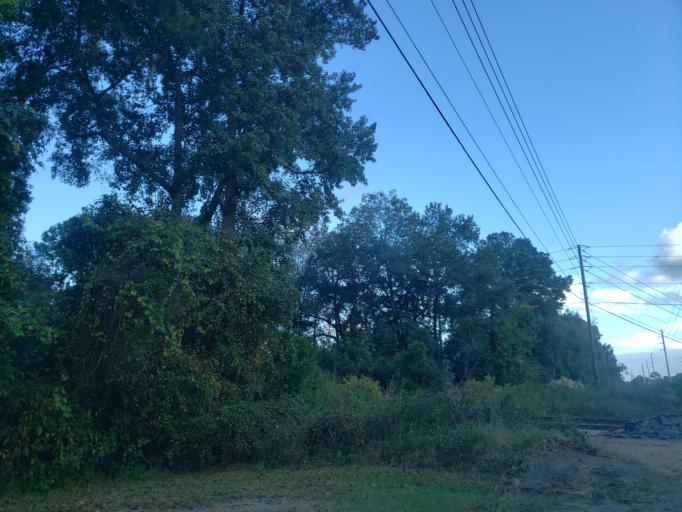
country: US
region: Georgia
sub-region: Chatham County
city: Georgetown
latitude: 31.9877
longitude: -81.2251
